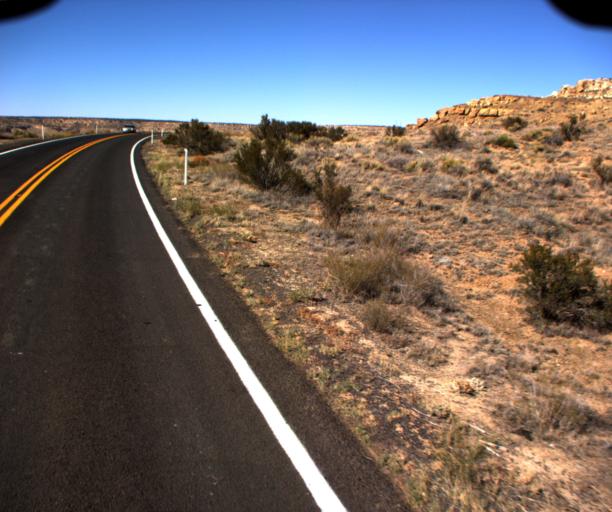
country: US
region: Arizona
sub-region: Navajo County
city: First Mesa
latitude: 35.8812
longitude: -110.6479
